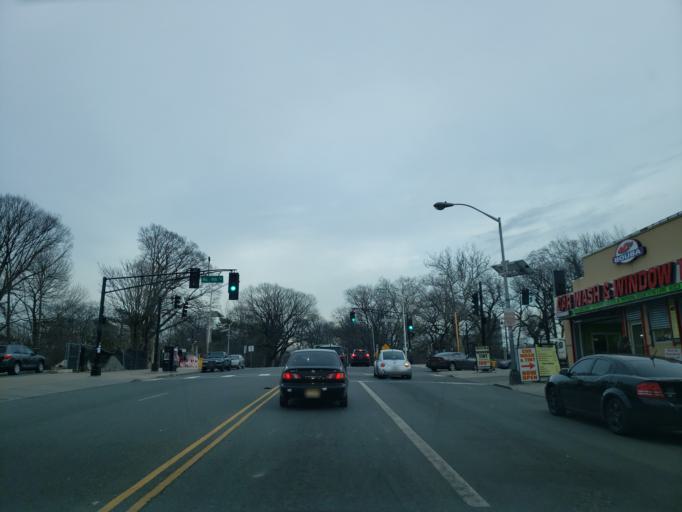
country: US
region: New Jersey
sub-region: Essex County
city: East Orange
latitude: 40.7588
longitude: -74.1857
